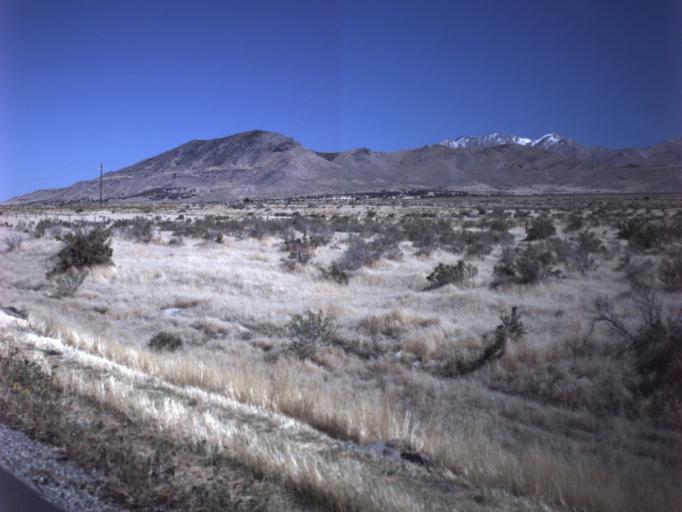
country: US
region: Utah
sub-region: Tooele County
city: Grantsville
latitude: 40.5098
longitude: -112.7478
